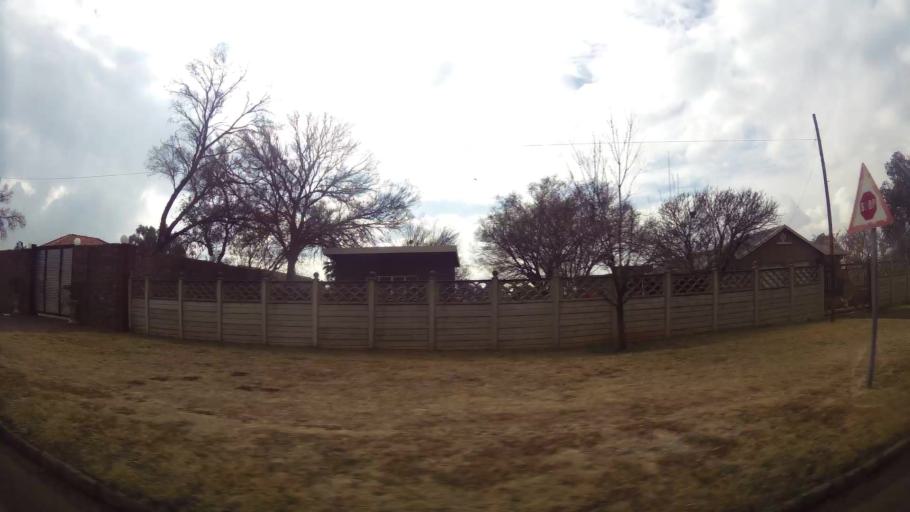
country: ZA
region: Gauteng
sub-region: Sedibeng District Municipality
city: Meyerton
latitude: -26.5995
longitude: 27.9943
